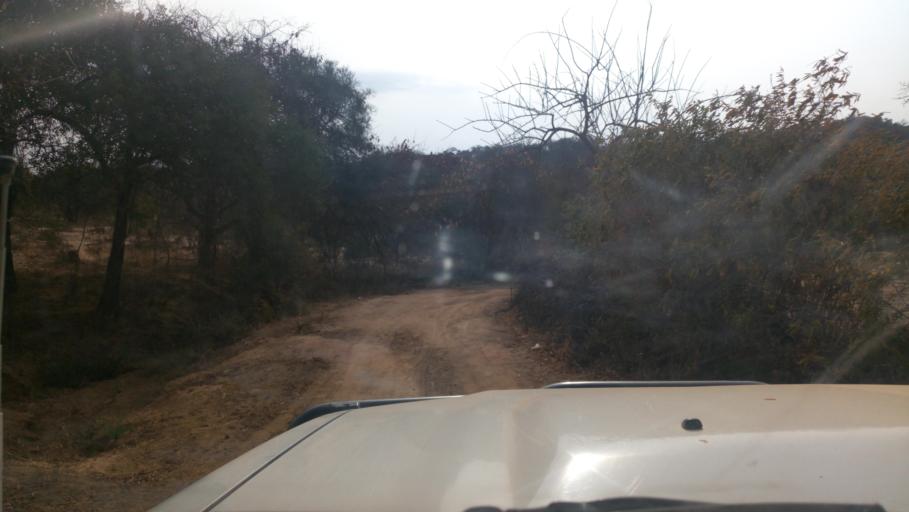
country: KE
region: Kitui
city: Kitui
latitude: -1.8026
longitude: 38.1897
